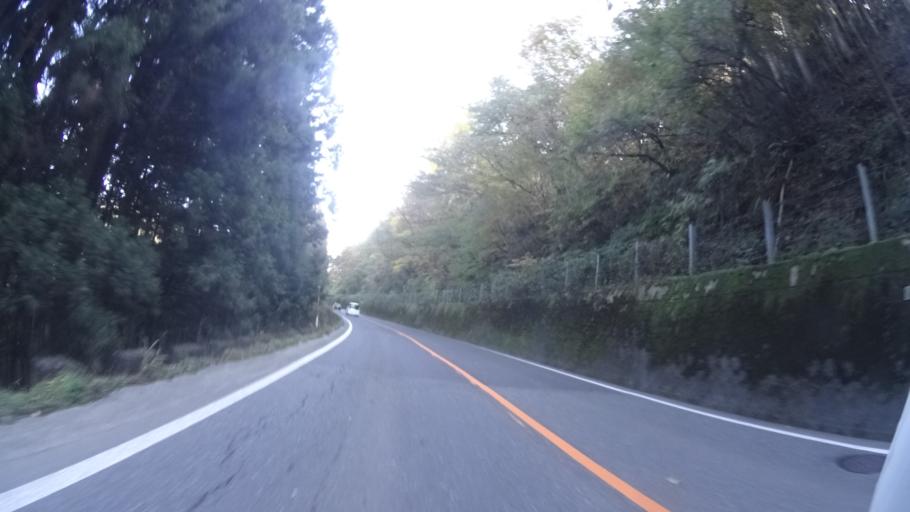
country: JP
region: Fukui
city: Ono
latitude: 35.9718
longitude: 136.5650
